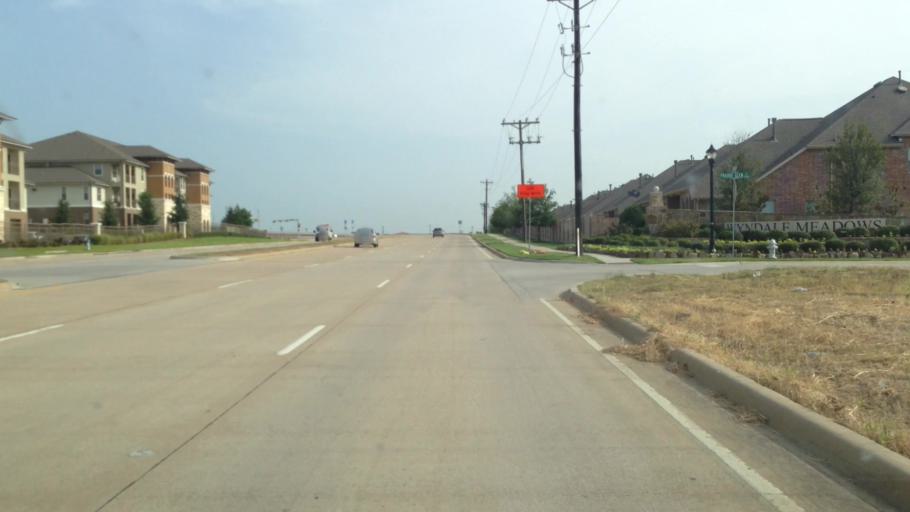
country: US
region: Texas
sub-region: Denton County
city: The Colony
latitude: 33.0479
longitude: -96.9185
